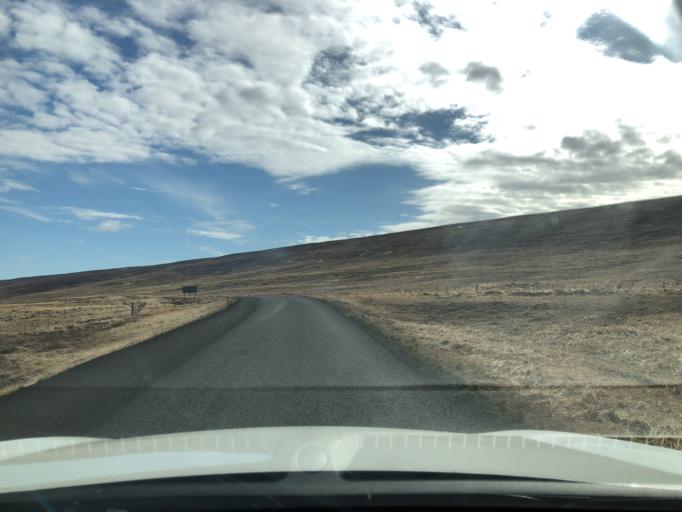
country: IS
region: West
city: Borgarnes
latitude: 65.0900
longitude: -21.7424
